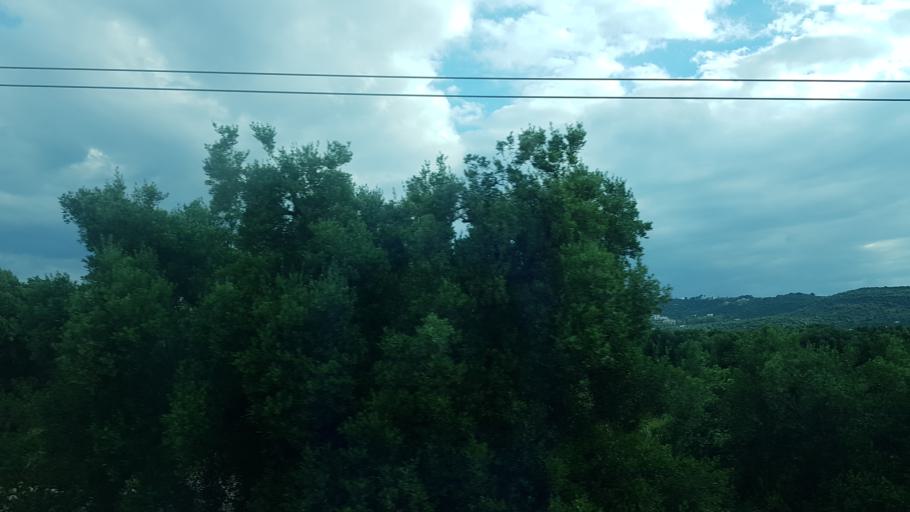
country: IT
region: Apulia
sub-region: Provincia di Brindisi
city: Ostuni
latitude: 40.7547
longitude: 17.5725
